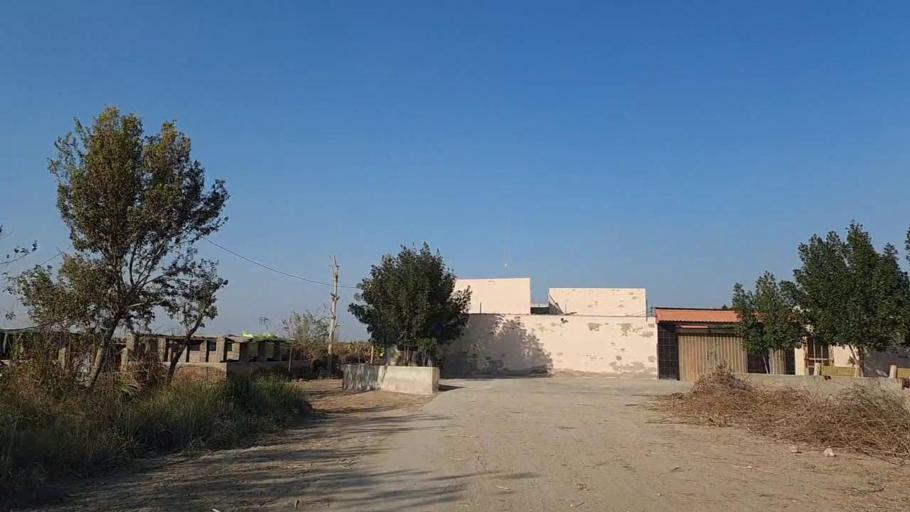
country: PK
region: Sindh
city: Bandhi
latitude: 26.6116
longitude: 68.3160
